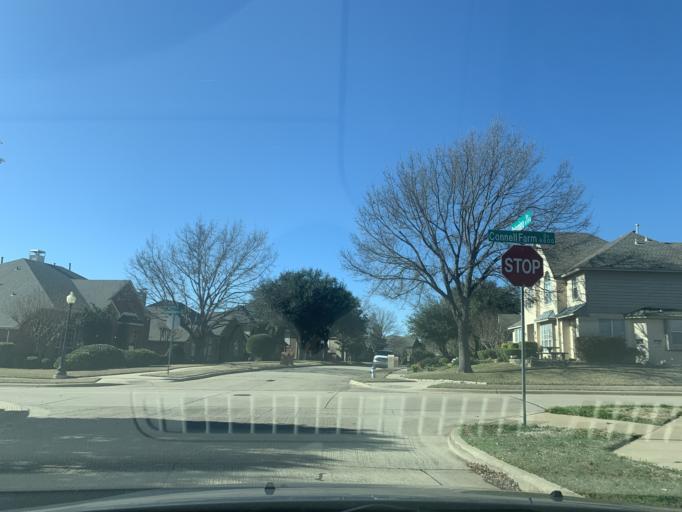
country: US
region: Texas
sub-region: Denton County
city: The Colony
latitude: 33.0628
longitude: -96.8357
